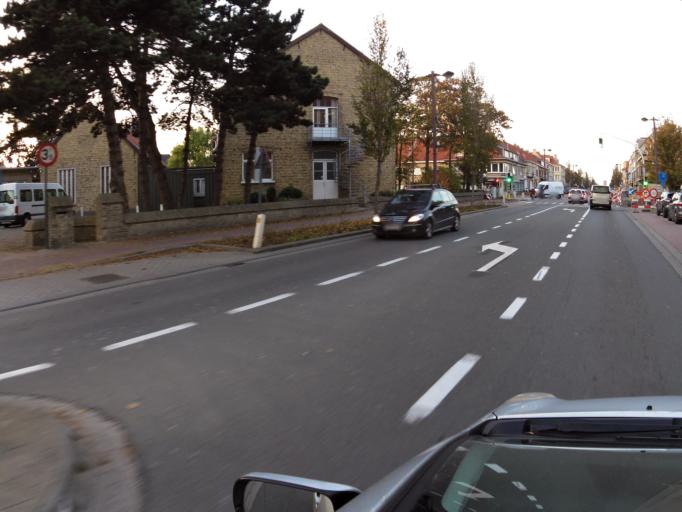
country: BE
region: Flanders
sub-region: Provincie West-Vlaanderen
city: Nieuwpoort
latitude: 51.1277
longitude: 2.7481
